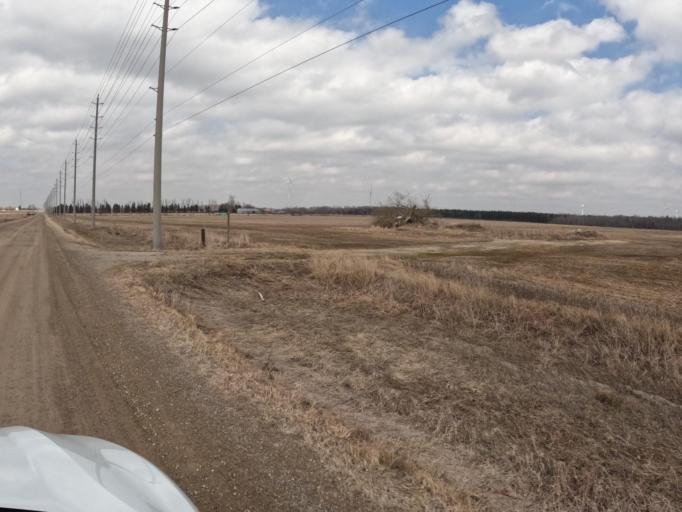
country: CA
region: Ontario
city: Shelburne
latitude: 44.0310
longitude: -80.3153
